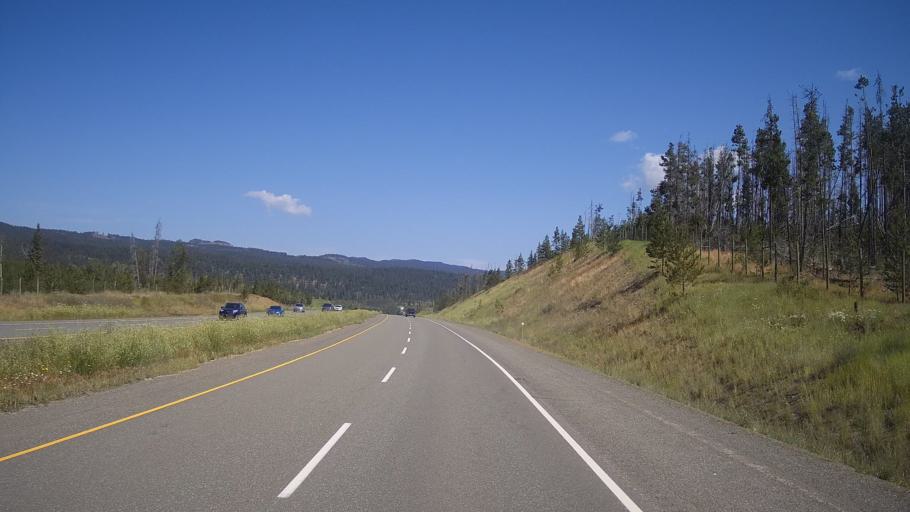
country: CA
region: British Columbia
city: Logan Lake
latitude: 50.4495
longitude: -120.5916
